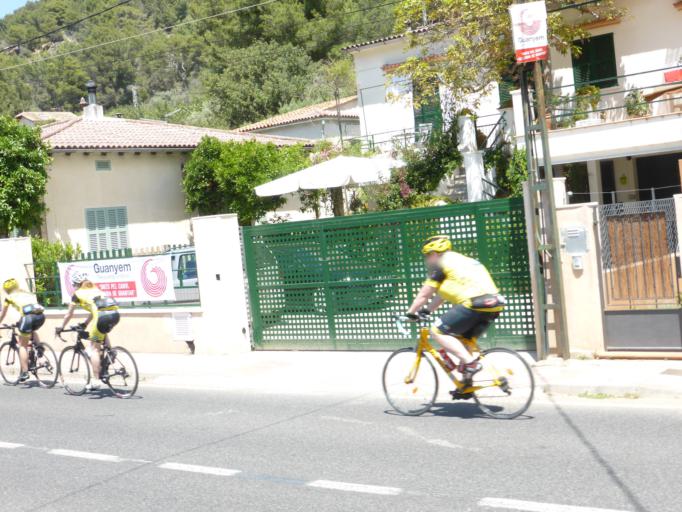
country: ES
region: Balearic Islands
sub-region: Illes Balears
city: Soller
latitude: 39.7884
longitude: 2.6955
